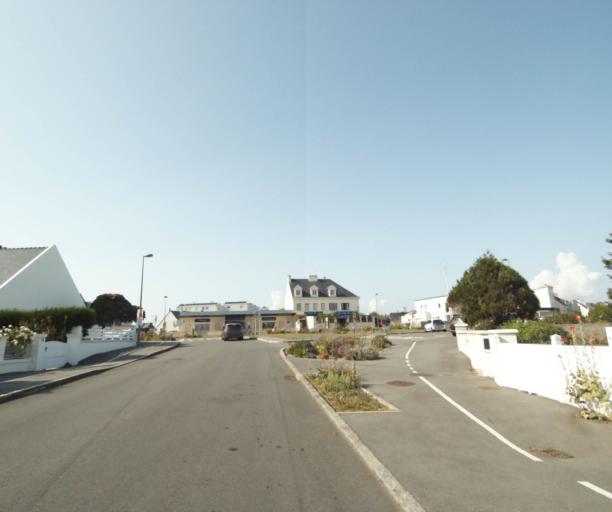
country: FR
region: Brittany
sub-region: Departement du Morbihan
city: Port-Louis
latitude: 47.7092
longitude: -3.3451
